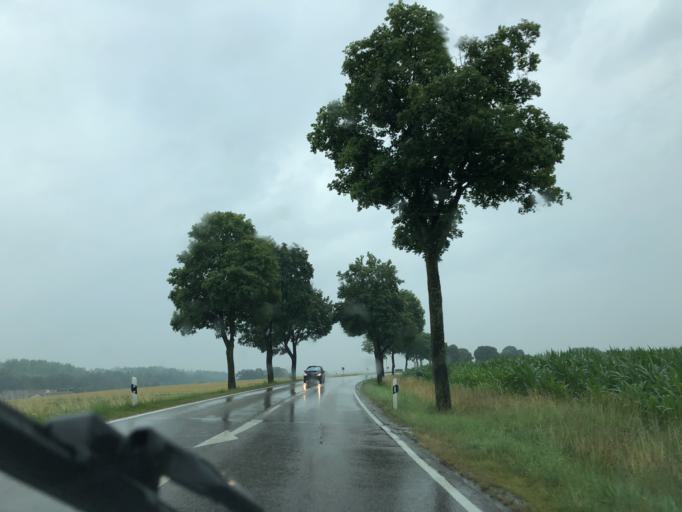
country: DE
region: Bavaria
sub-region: Upper Bavaria
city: Zolling
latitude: 48.4638
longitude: 11.7660
